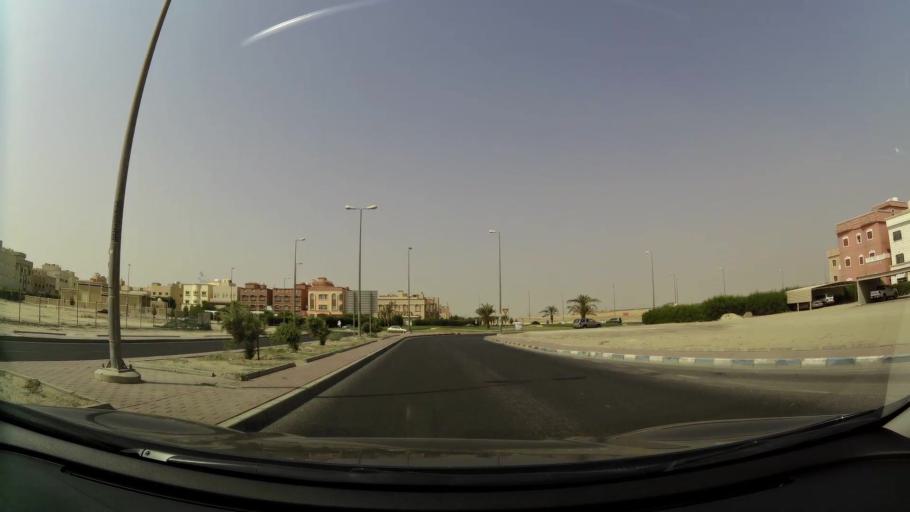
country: KW
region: Muhafazat al Jahra'
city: Al Jahra'
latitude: 29.3080
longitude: 47.7058
